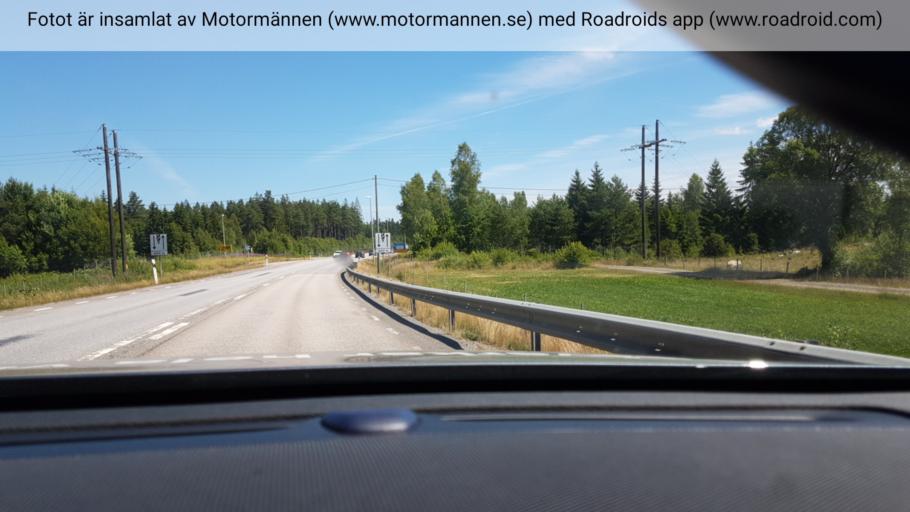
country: SE
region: Kronoberg
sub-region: Alvesta Kommun
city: Alvesta
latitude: 56.9122
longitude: 14.4808
